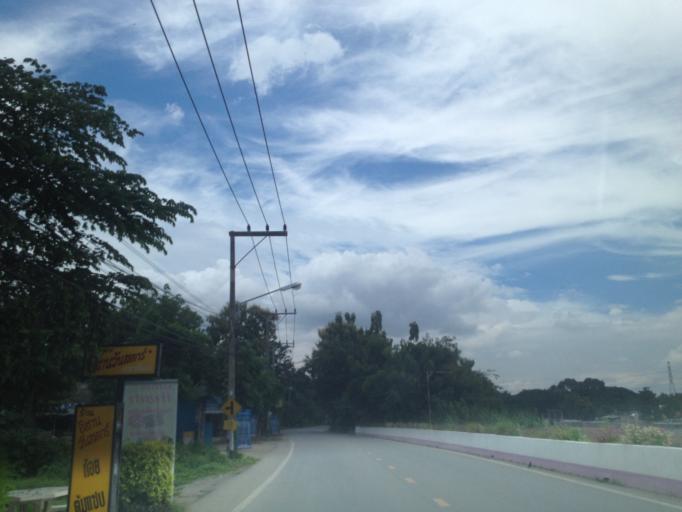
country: TH
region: Chiang Mai
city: Saraphi
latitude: 18.7216
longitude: 98.9861
